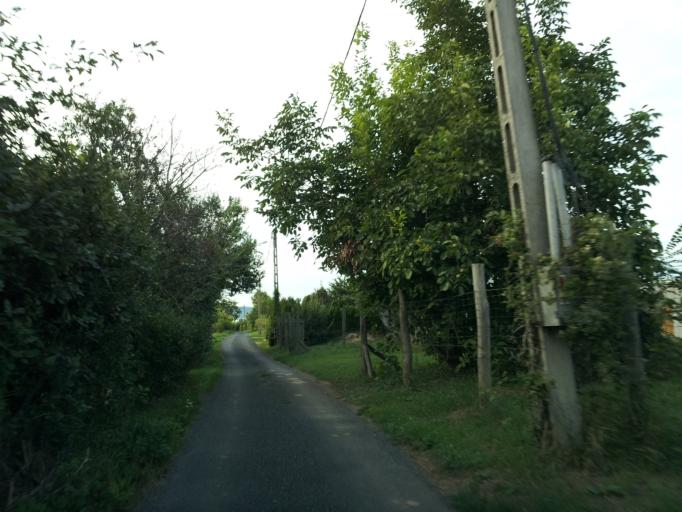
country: HU
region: Somogy
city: Zamardi
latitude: 46.8712
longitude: 17.9301
